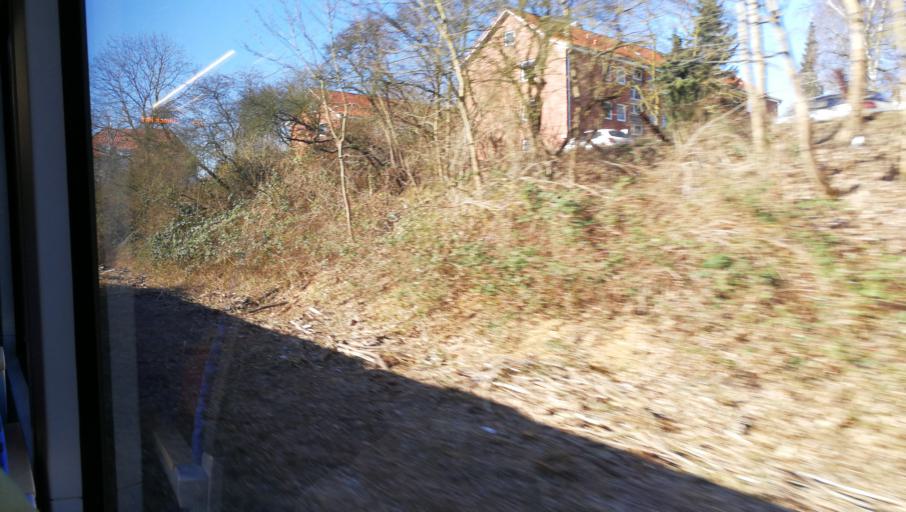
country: DE
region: Schleswig-Holstein
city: Luebeck
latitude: 53.8426
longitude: 10.6828
